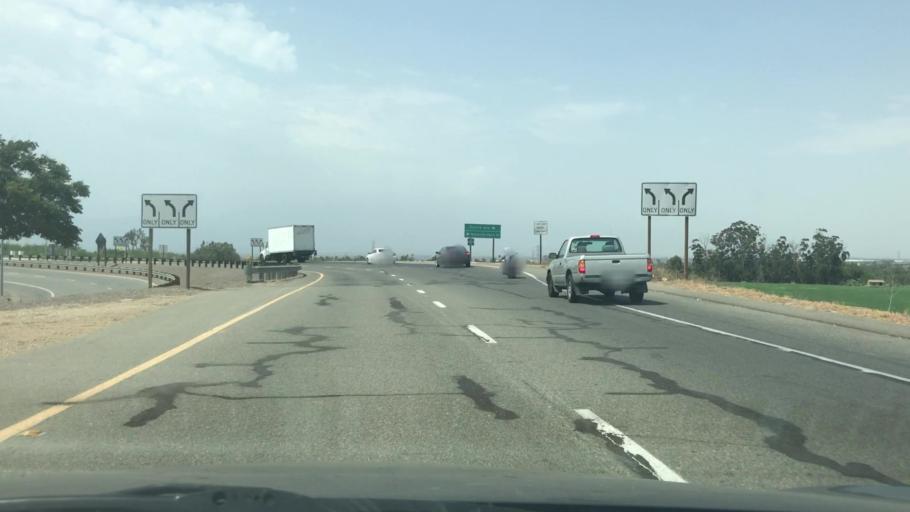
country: US
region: California
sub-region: San Bernardino County
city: Los Serranos
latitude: 33.9301
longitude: -117.6576
